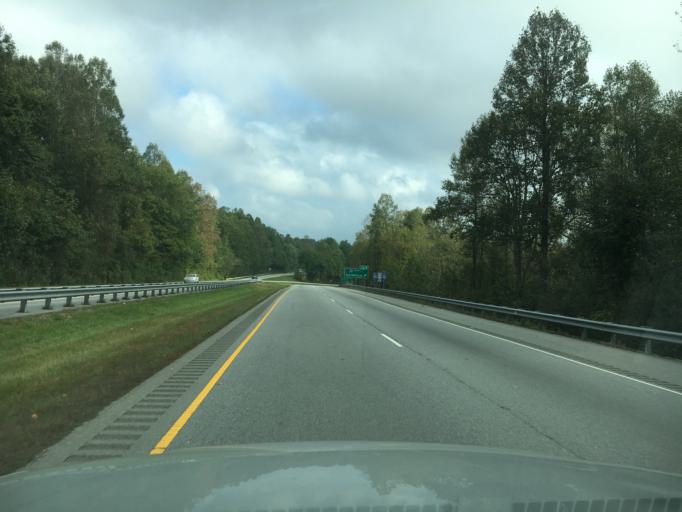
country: US
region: North Carolina
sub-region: Henderson County
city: East Flat Rock
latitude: 35.2782
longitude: -82.4018
